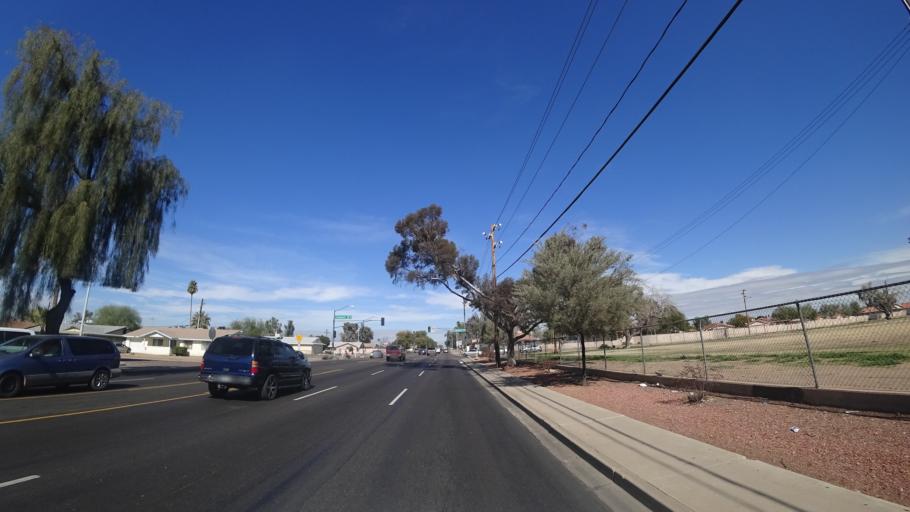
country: US
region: Arizona
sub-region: Maricopa County
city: Glendale
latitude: 33.5013
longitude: -112.2031
